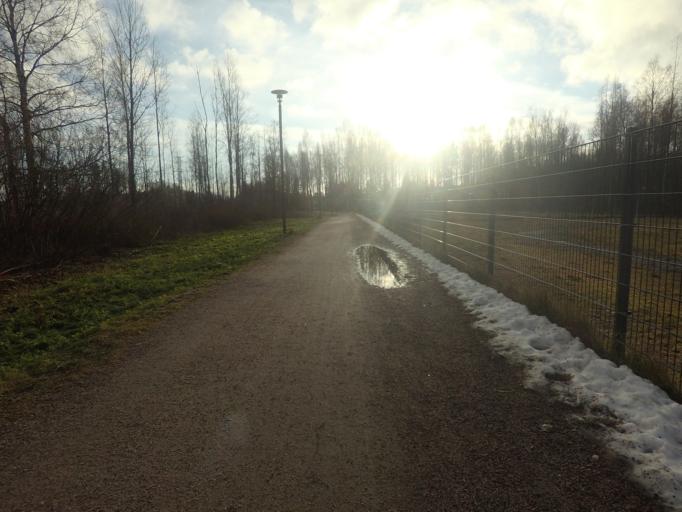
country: FI
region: Uusimaa
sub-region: Helsinki
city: Kilo
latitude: 60.1989
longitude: 24.7735
